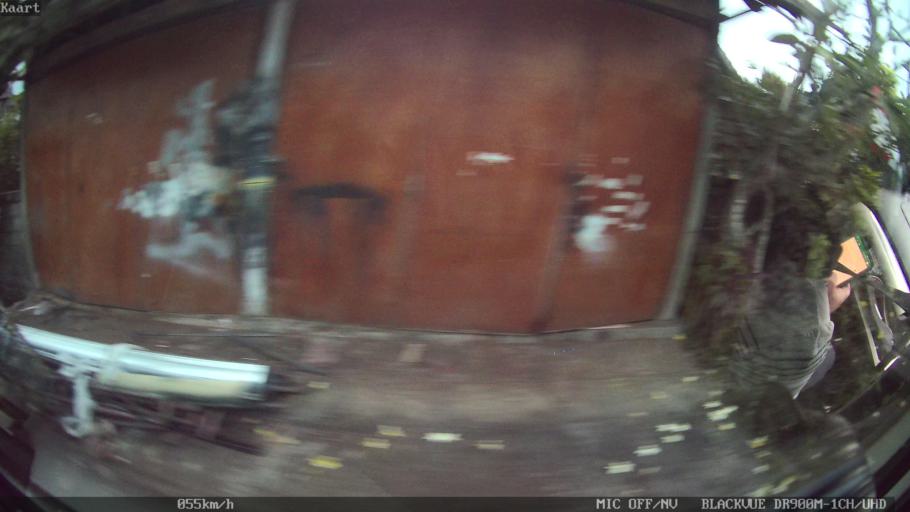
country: ID
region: Bali
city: Banjar Pekenjelodan
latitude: -8.5619
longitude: 115.1782
